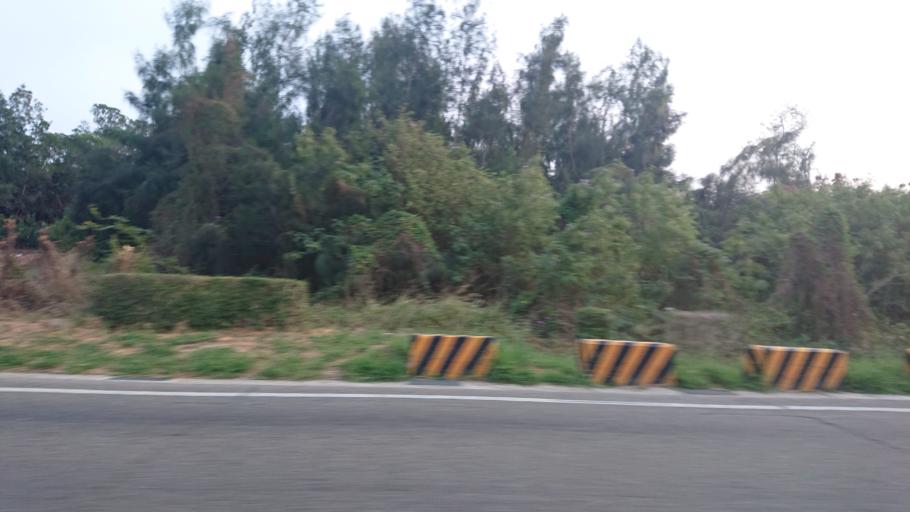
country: TW
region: Fukien
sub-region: Kinmen
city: Jincheng
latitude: 24.4521
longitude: 118.3511
